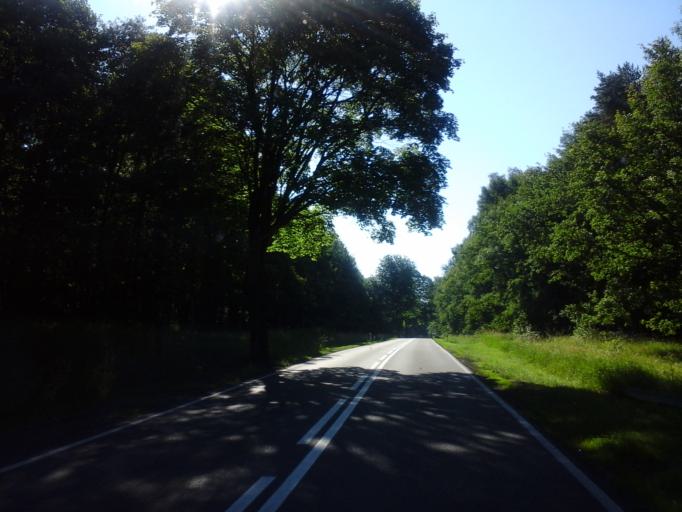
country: PL
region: West Pomeranian Voivodeship
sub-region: Powiat drawski
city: Drawsko Pomorskie
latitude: 53.4950
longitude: 15.6992
